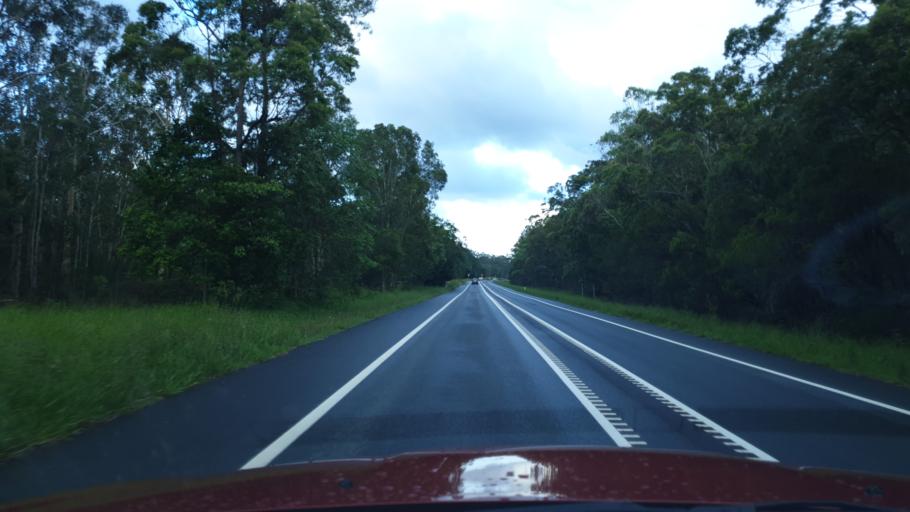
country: AU
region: Queensland
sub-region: Sunshine Coast
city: Little Mountain
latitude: -26.8026
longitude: 152.9820
